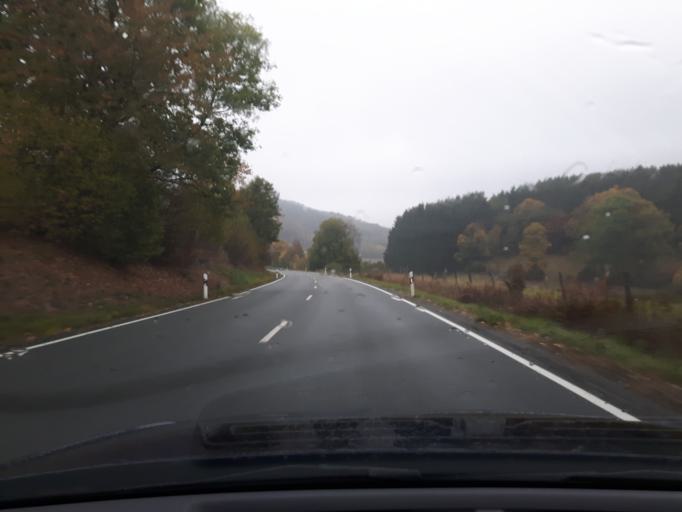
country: DE
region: North Rhine-Westphalia
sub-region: Regierungsbezirk Arnsberg
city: Bad Berleburg
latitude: 50.9942
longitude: 8.3947
